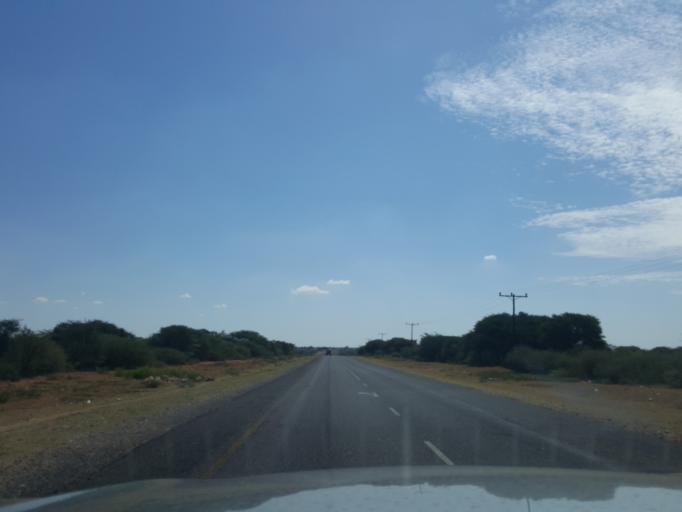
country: BW
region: Kweneng
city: Letlhakeng
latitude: -24.1195
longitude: 25.0659
